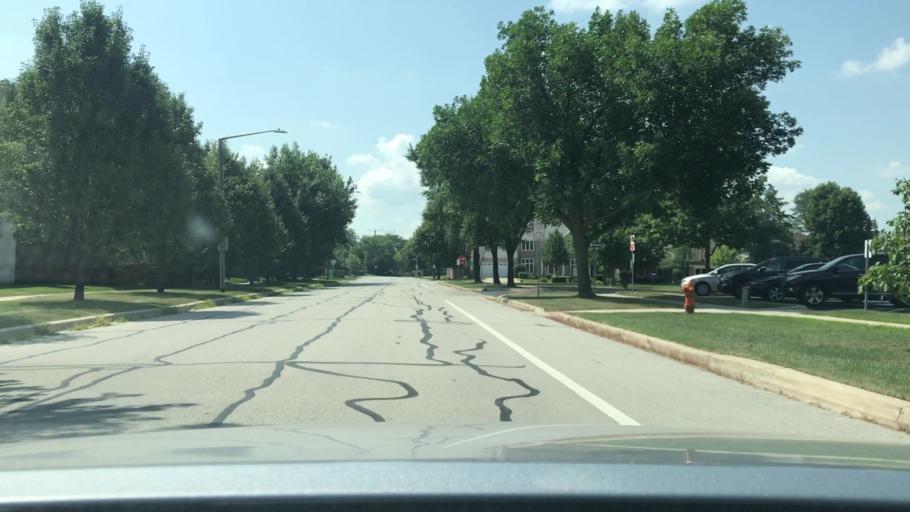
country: US
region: Illinois
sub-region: DuPage County
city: Woodridge
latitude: 41.7395
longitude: -88.0955
